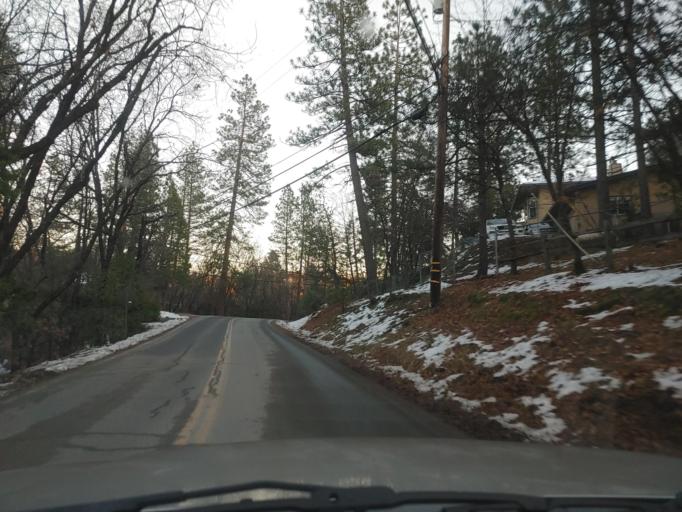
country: US
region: California
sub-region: Tuolumne County
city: Twain Harte
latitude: 38.0288
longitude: -120.2593
